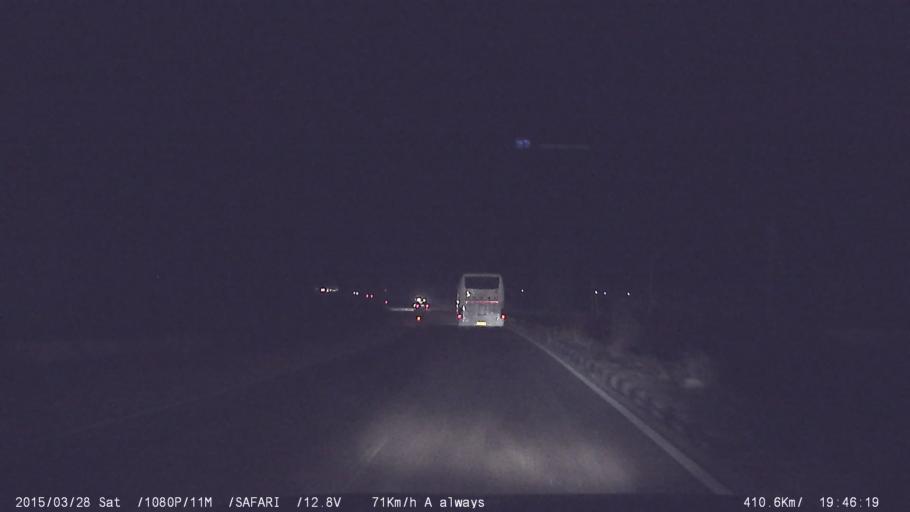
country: IN
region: Karnataka
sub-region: Mandya
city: Pandavapura
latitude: 12.4850
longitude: 76.7786
